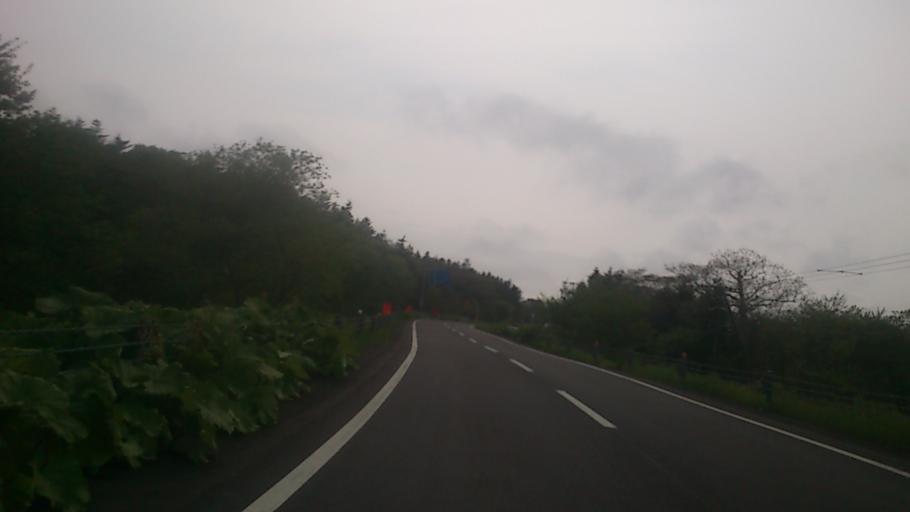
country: JP
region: Hokkaido
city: Nemuro
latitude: 43.2065
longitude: 145.3293
